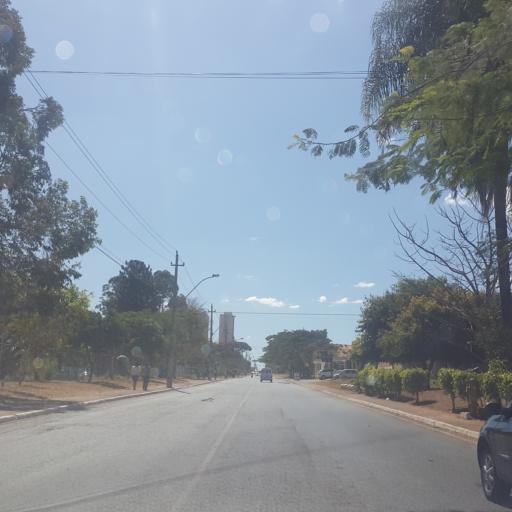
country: BR
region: Federal District
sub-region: Brasilia
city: Brasilia
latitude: -15.8181
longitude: -48.0704
